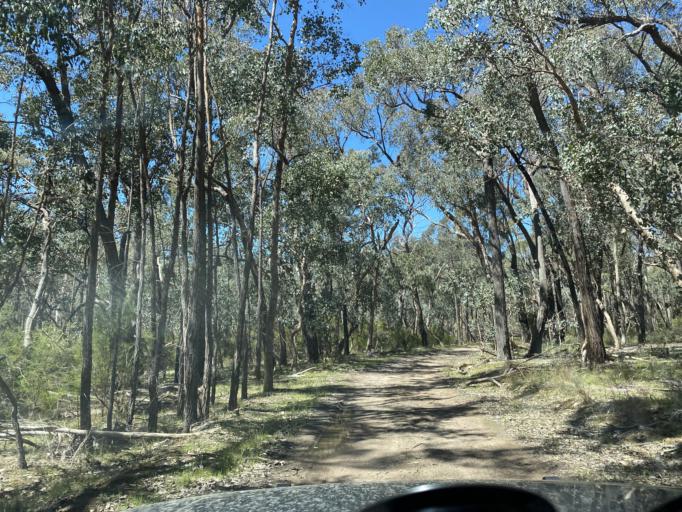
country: AU
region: Victoria
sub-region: Benalla
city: Benalla
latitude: -36.7021
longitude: 146.1519
